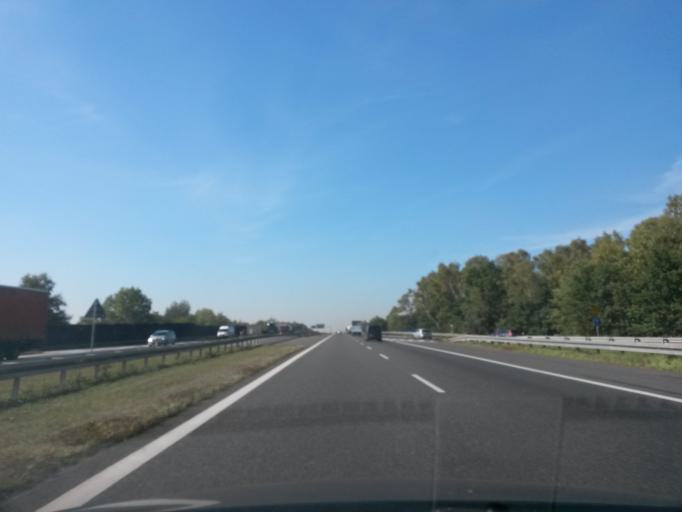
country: PL
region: Silesian Voivodeship
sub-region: Myslowice
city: Myslowice
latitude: 50.2085
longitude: 19.1639
